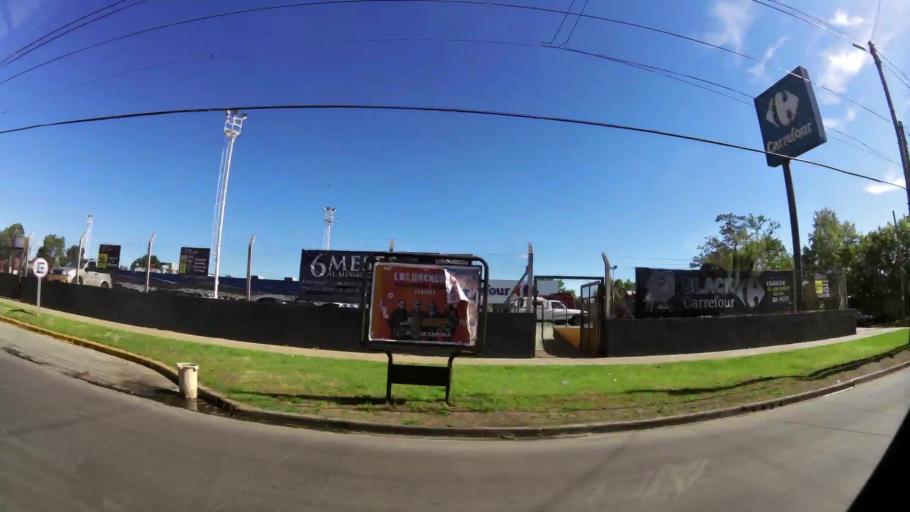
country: AR
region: Buenos Aires
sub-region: Partido de Lomas de Zamora
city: Lomas de Zamora
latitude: -34.7481
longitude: -58.4116
